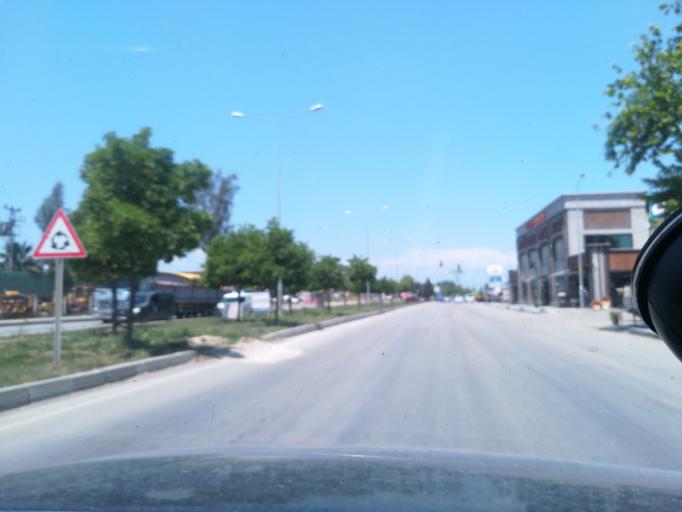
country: TR
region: Adana
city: Seyhan
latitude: 36.9900
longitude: 35.2530
